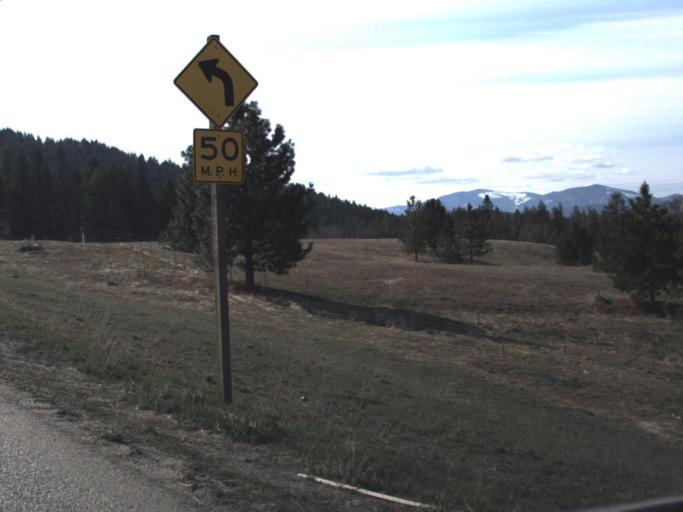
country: US
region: Washington
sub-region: Stevens County
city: Colville
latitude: 48.5459
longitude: -117.8552
